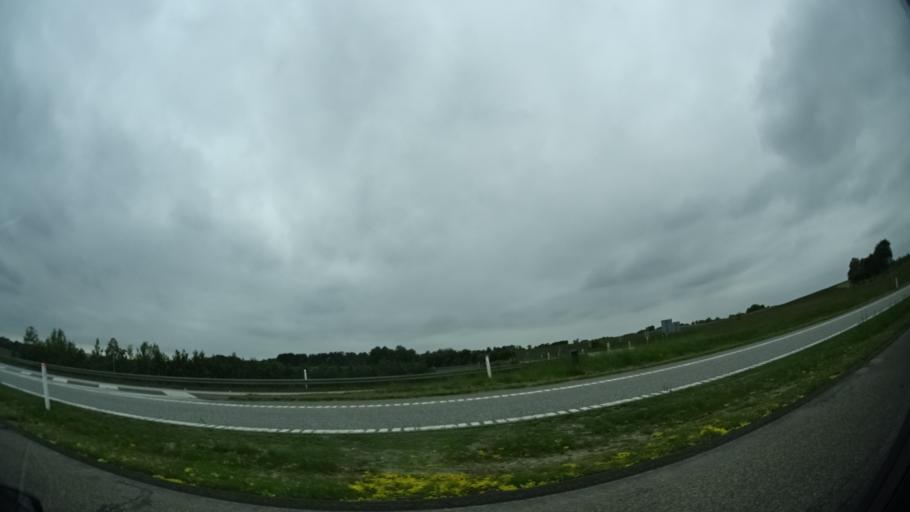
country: DK
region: Central Jutland
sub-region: Arhus Kommune
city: Framlev
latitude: 56.1585
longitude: 10.0451
